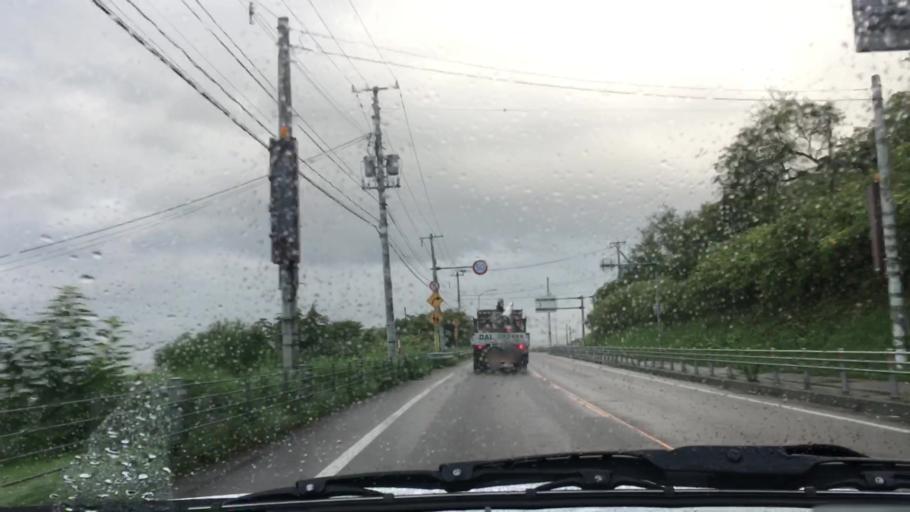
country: JP
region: Hokkaido
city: Nanae
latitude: 42.1560
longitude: 140.4798
